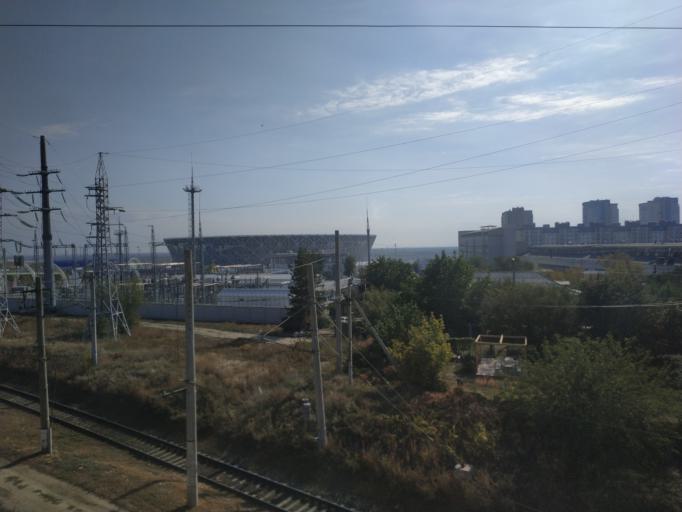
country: RU
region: Volgograd
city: Volgograd
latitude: 48.7360
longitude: 44.5396
